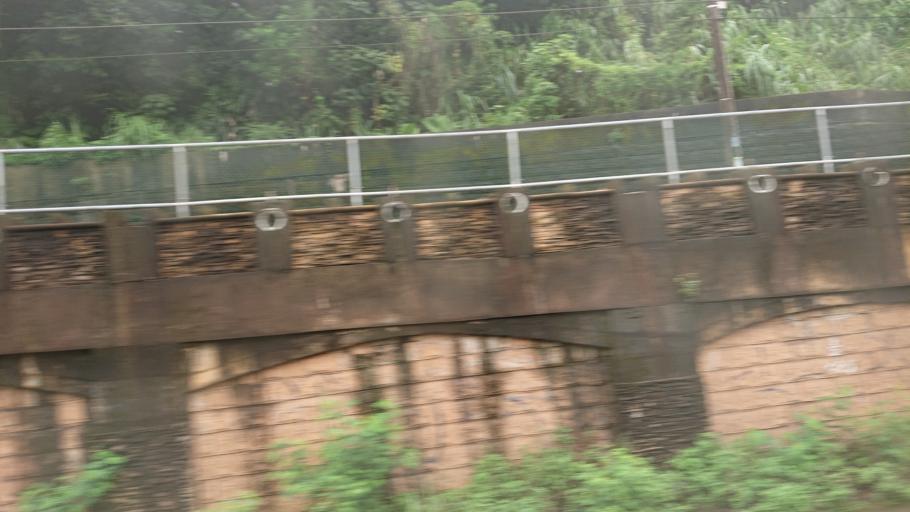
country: TW
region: Taiwan
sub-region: Keelung
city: Keelung
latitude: 25.0839
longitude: 121.7049
